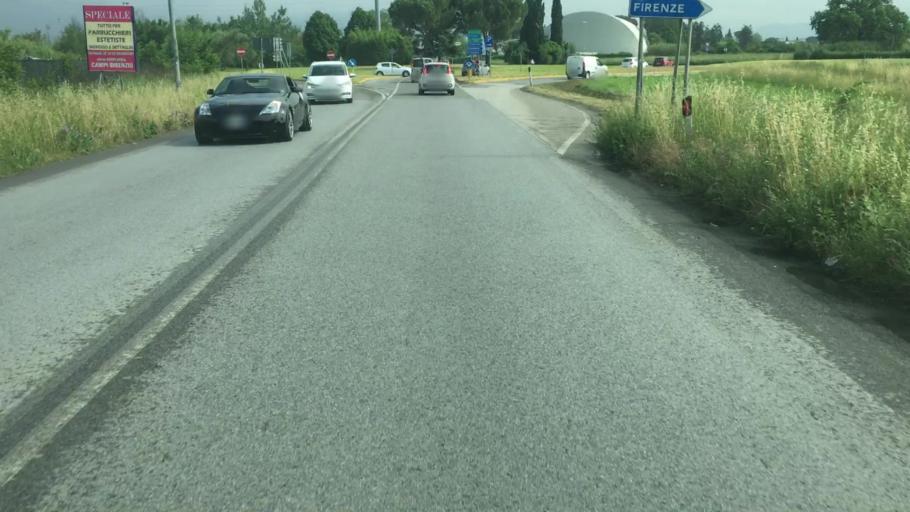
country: IT
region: Tuscany
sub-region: Province of Florence
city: Campi Bisenzio
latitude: 43.8147
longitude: 11.1203
